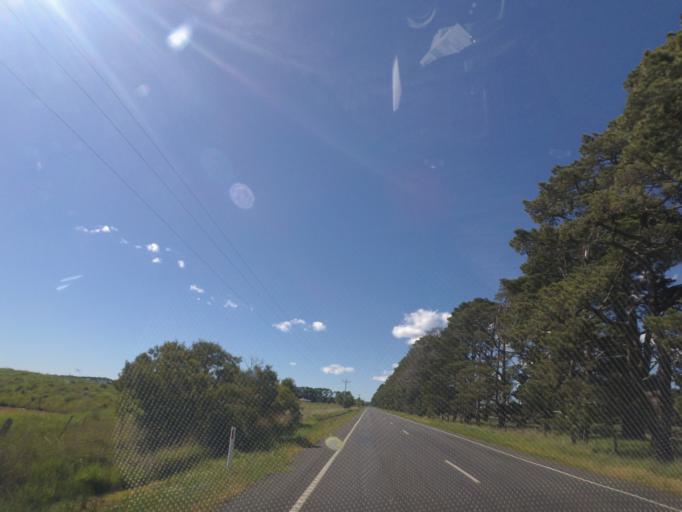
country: AU
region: Victoria
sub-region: Moorabool
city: Bacchus Marsh
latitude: -37.6927
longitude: 144.2250
